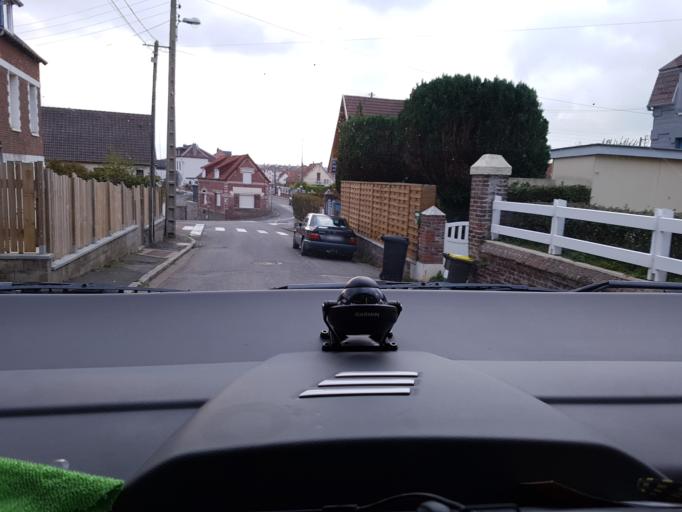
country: FR
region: Haute-Normandie
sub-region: Departement de la Seine-Maritime
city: Dieppe
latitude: 49.9313
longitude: 1.0928
